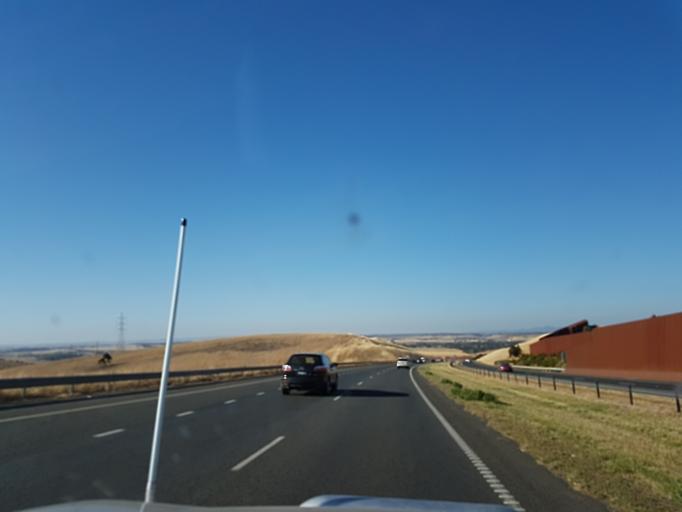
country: AU
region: Victoria
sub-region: Greater Geelong
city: Wandana Heights
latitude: -38.1660
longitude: 144.2919
